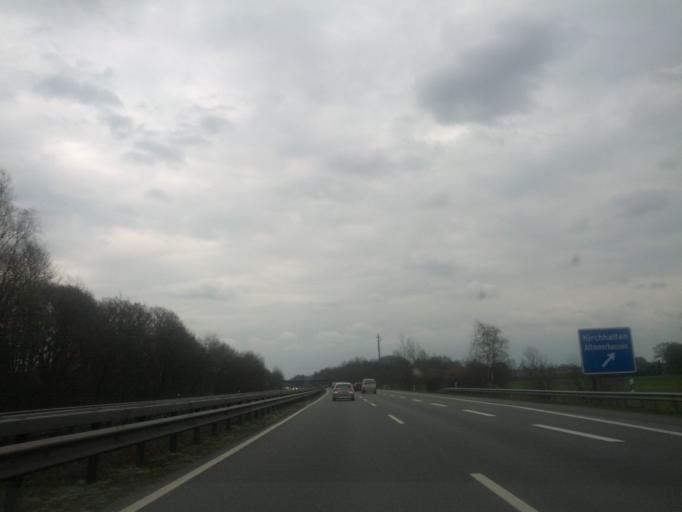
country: DE
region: Lower Saxony
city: Hatten
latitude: 53.0646
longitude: 8.3459
